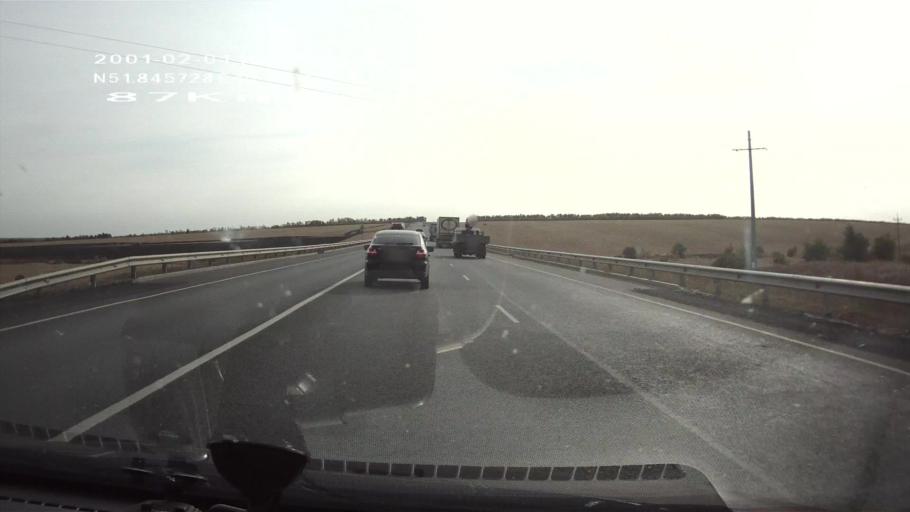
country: RU
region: Saratov
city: Yelshanka
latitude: 51.8456
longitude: 46.4836
